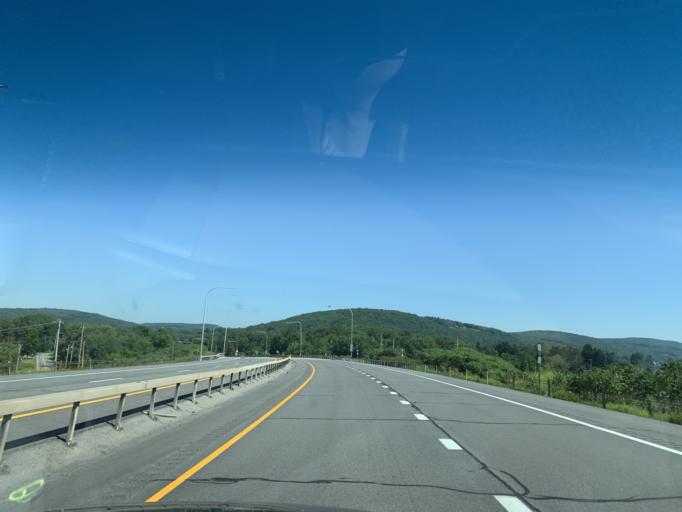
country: US
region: New York
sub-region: Delaware County
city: Sidney
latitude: 42.3051
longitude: -75.4032
